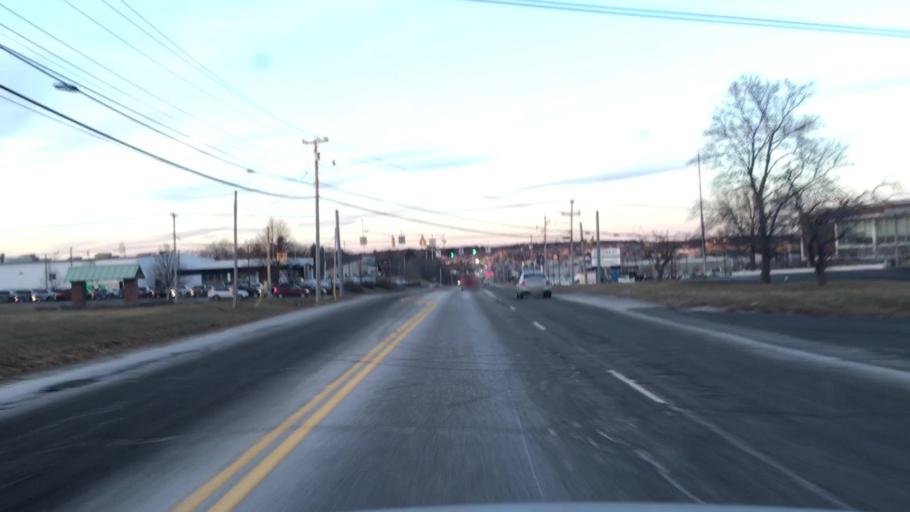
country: US
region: Maine
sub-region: Penobscot County
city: Brewer
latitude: 44.8215
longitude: -68.7393
